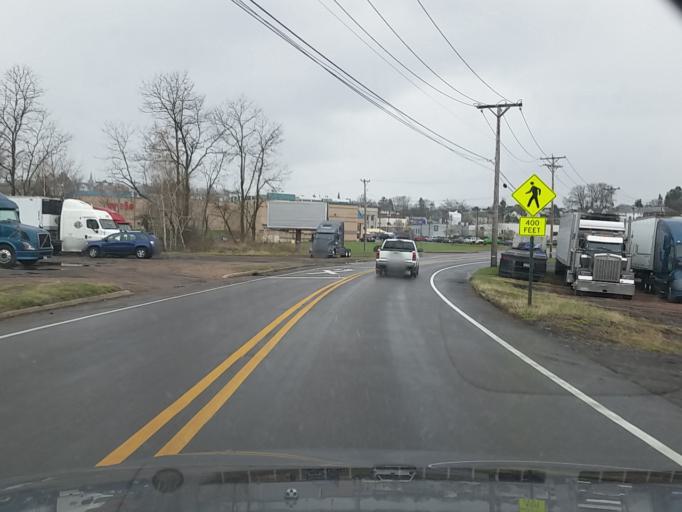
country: US
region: Pennsylvania
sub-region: Luzerne County
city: Nanticoke
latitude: 41.2088
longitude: -76.0038
